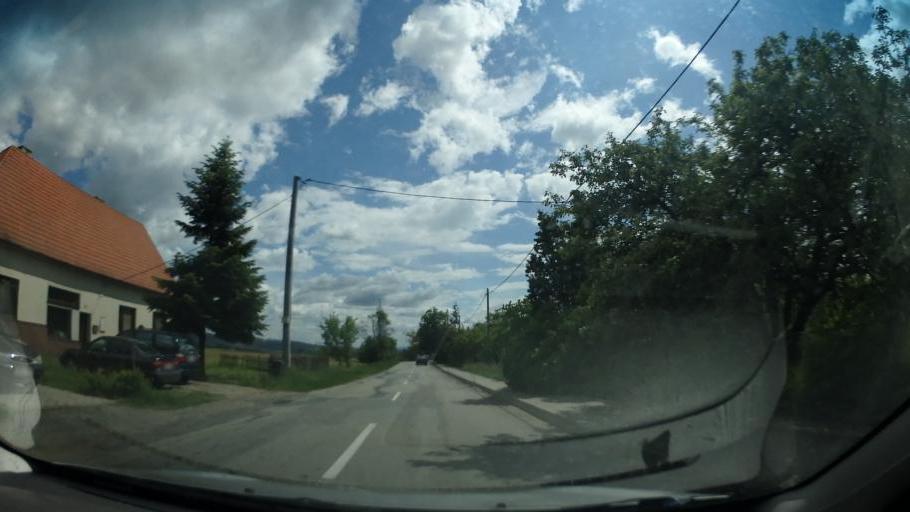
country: CZ
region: South Moravian
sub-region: Okres Blansko
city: Letovice
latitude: 49.5929
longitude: 16.5949
